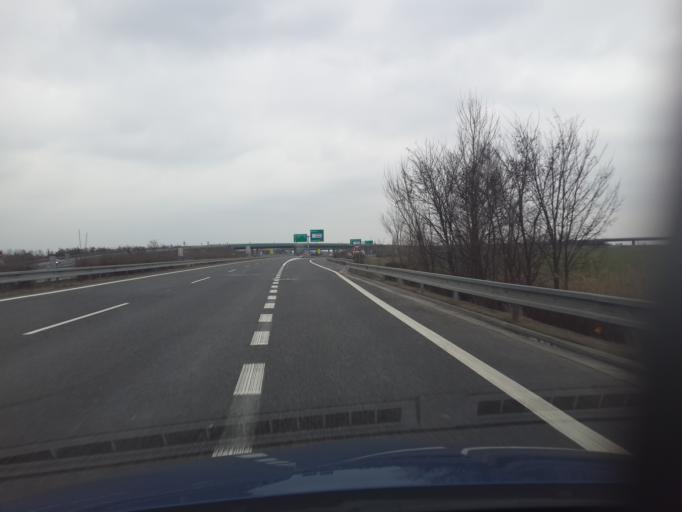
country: AT
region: Burgenland
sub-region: Politischer Bezirk Neusiedl am See
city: Kittsee
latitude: 48.0780
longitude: 17.1010
